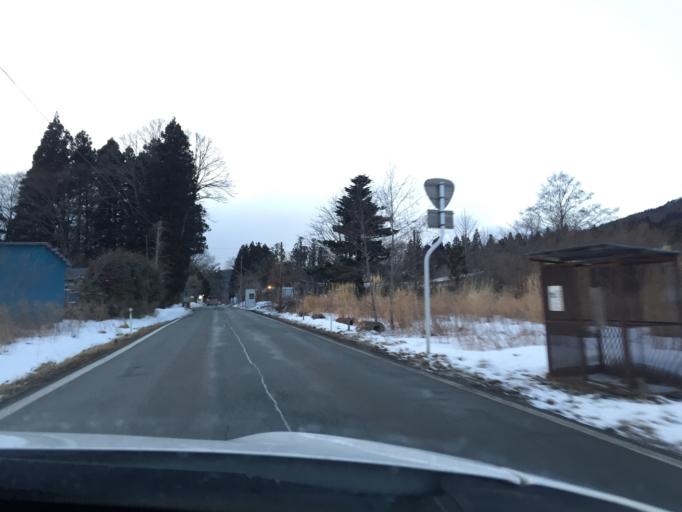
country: JP
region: Fukushima
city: Funehikimachi-funehiki
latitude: 37.5811
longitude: 140.7213
